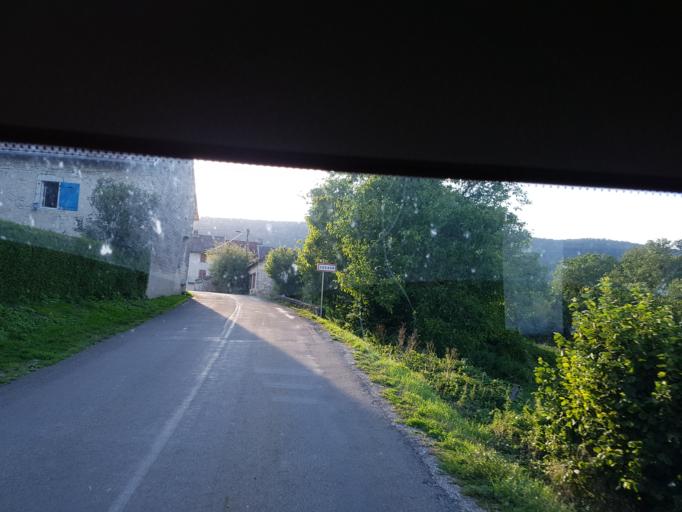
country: FR
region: Franche-Comte
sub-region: Departement du Jura
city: Moirans-en-Montagne
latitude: 46.4025
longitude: 5.6530
